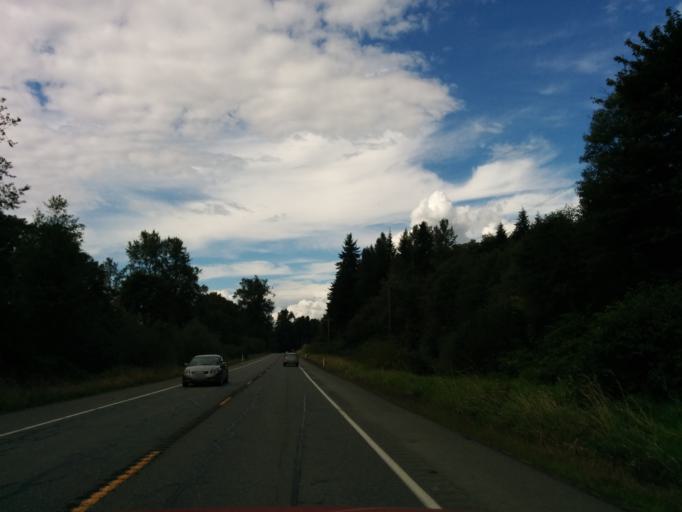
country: US
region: Washington
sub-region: Snohomish County
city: Monroe
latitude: 47.8061
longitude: -121.9808
